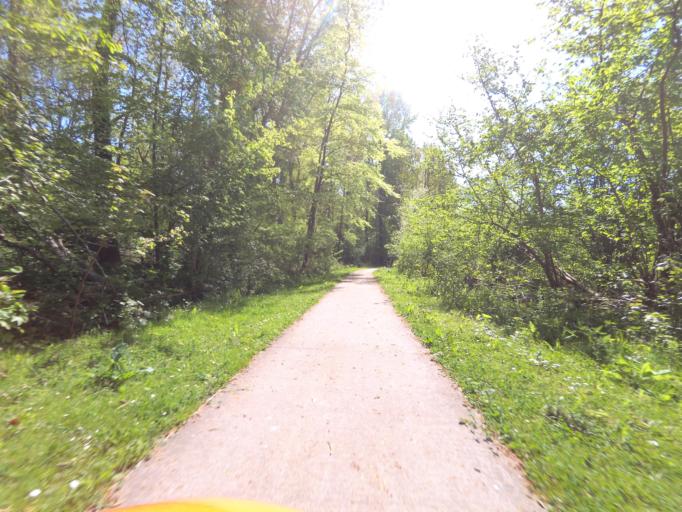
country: NL
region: Gelderland
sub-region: Gemeente Harderwijk
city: Harderwijk
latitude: 52.3913
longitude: 5.6294
